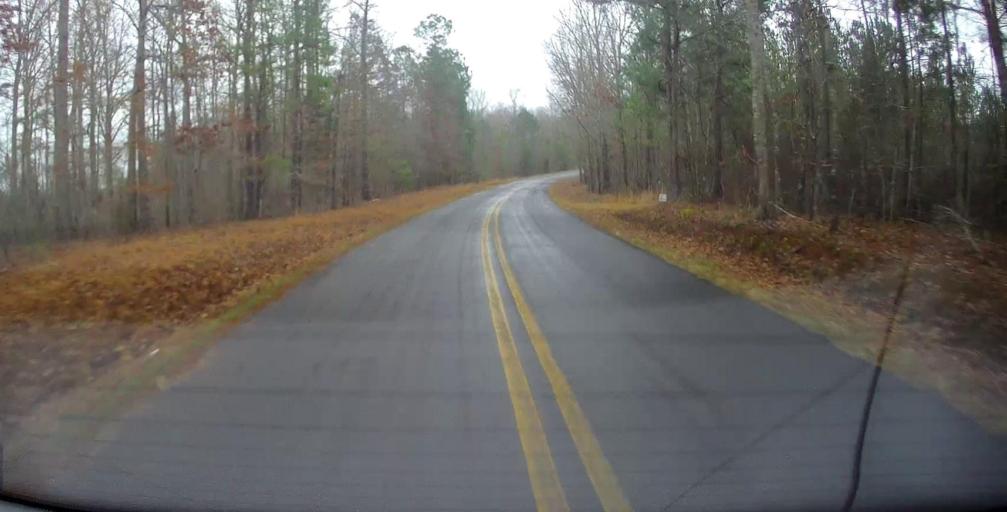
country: US
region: Georgia
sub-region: Monroe County
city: Forsyth
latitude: 33.0866
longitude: -83.8956
